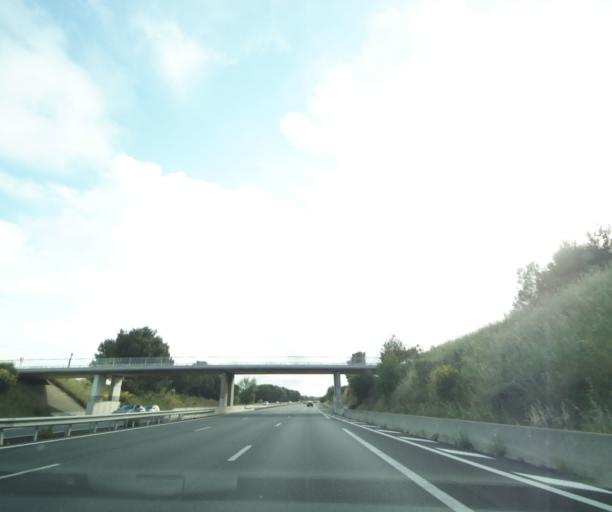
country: FR
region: Languedoc-Roussillon
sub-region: Departement de l'Herault
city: Meze
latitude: 43.4267
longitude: 3.5566
